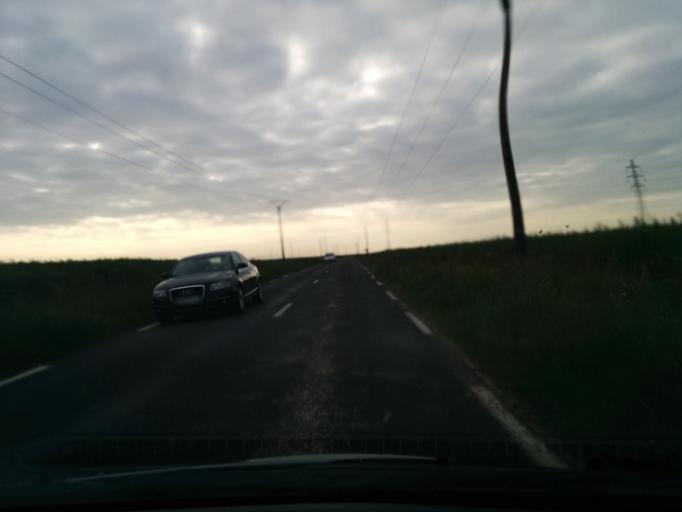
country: FR
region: Ile-de-France
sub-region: Departement des Yvelines
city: Limetz-Villez
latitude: 49.0946
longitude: 1.5352
